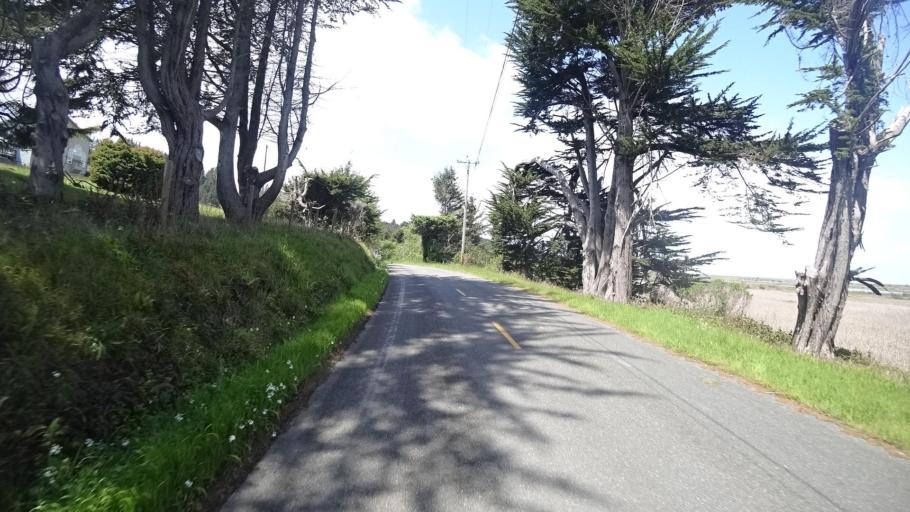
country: US
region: California
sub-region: Humboldt County
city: Humboldt Hill
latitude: 40.6746
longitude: -124.2204
